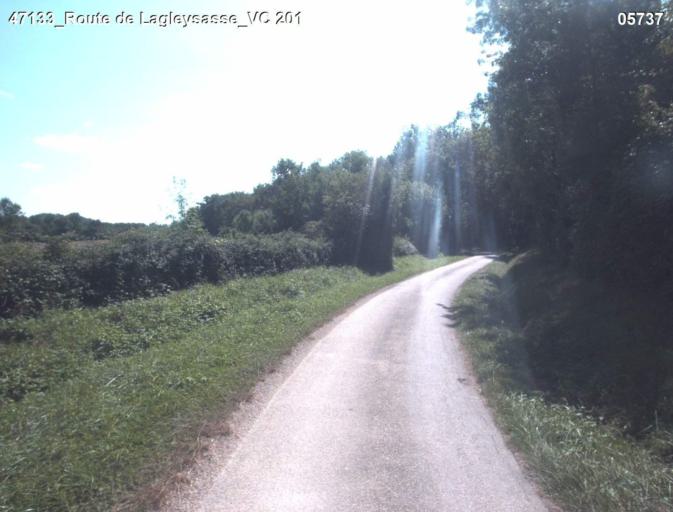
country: FR
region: Aquitaine
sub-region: Departement du Lot-et-Garonne
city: Laplume
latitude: 44.0666
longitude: 0.4949
